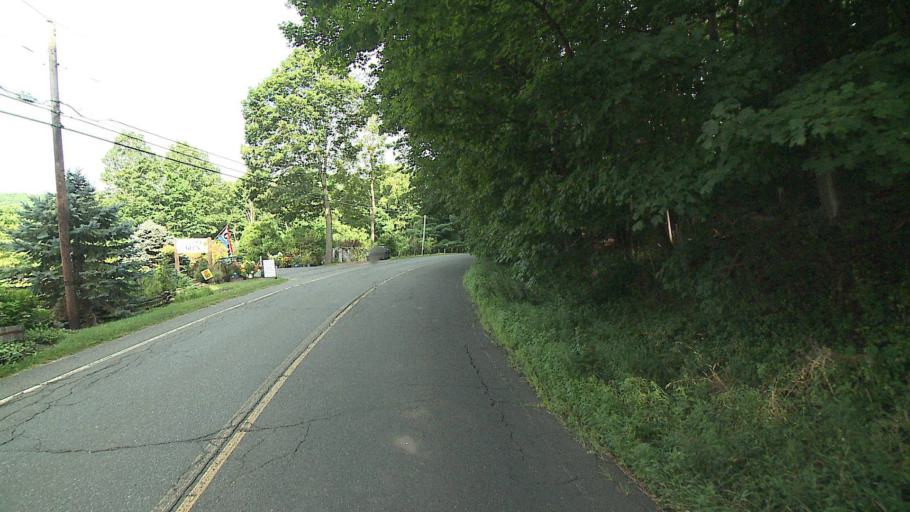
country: US
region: New York
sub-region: Putnam County
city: Putnam Lake
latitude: 41.4906
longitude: -73.5271
